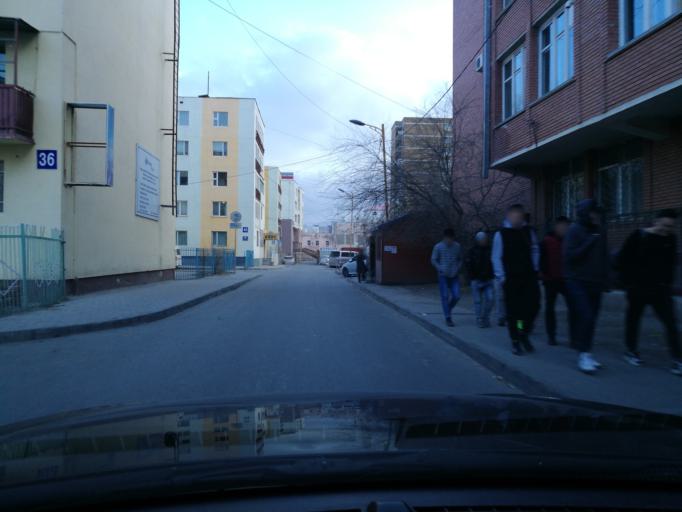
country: MN
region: Ulaanbaatar
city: Ulaanbaatar
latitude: 47.9222
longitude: 106.9257
